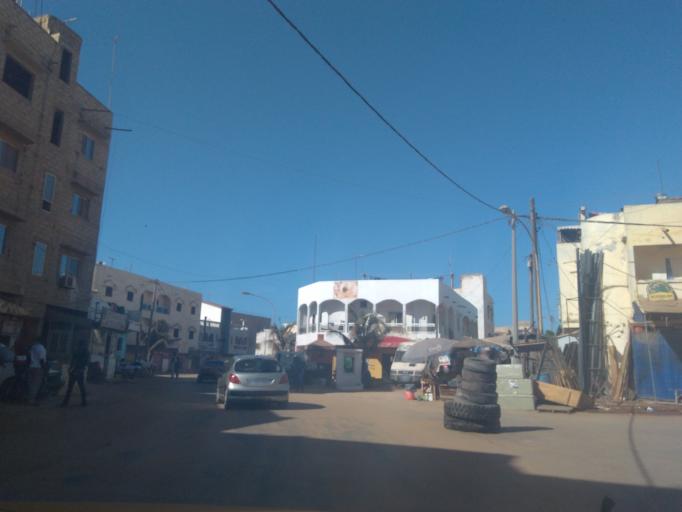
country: SN
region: Dakar
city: Pikine
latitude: 14.7716
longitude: -17.4220
